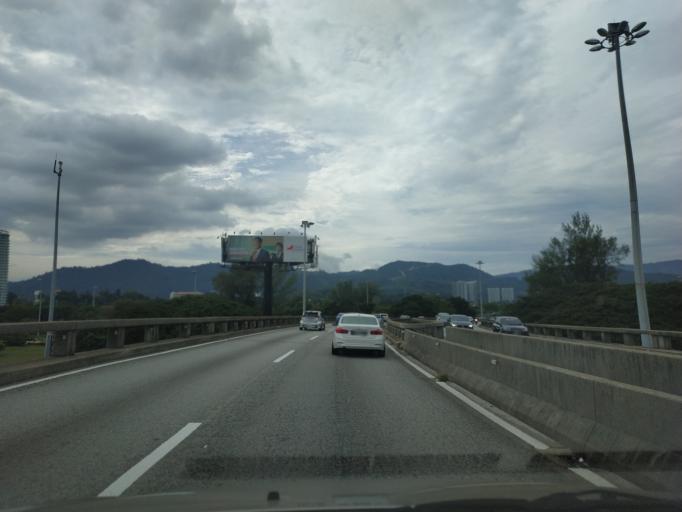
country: MY
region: Penang
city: Kampung Sungai Ara
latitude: 5.3586
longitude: 100.3165
